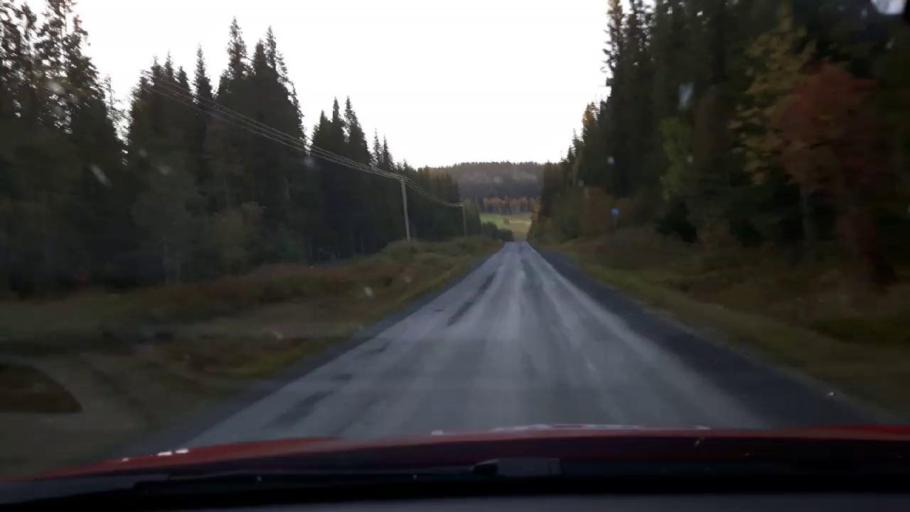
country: SE
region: Jaemtland
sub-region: Krokoms Kommun
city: Krokom
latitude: 63.4811
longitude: 14.2117
